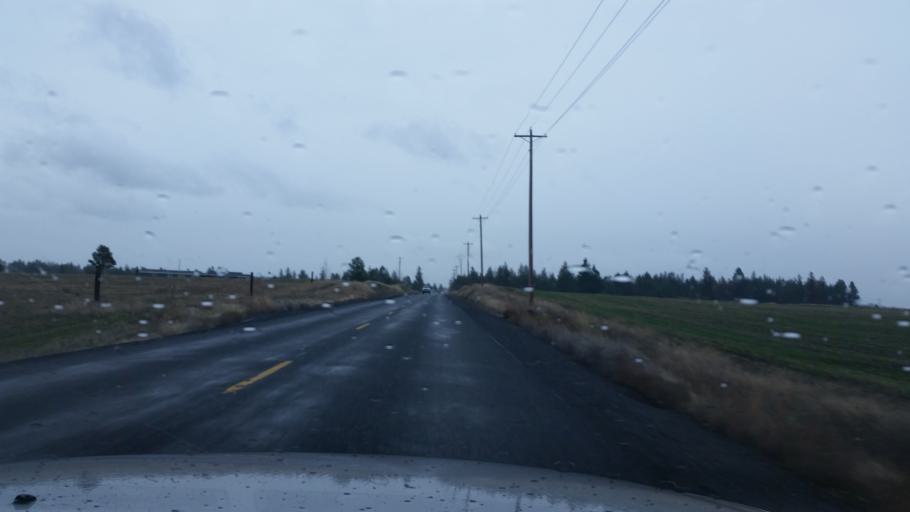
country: US
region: Washington
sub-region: Spokane County
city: Airway Heights
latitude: 47.6719
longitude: -117.5951
